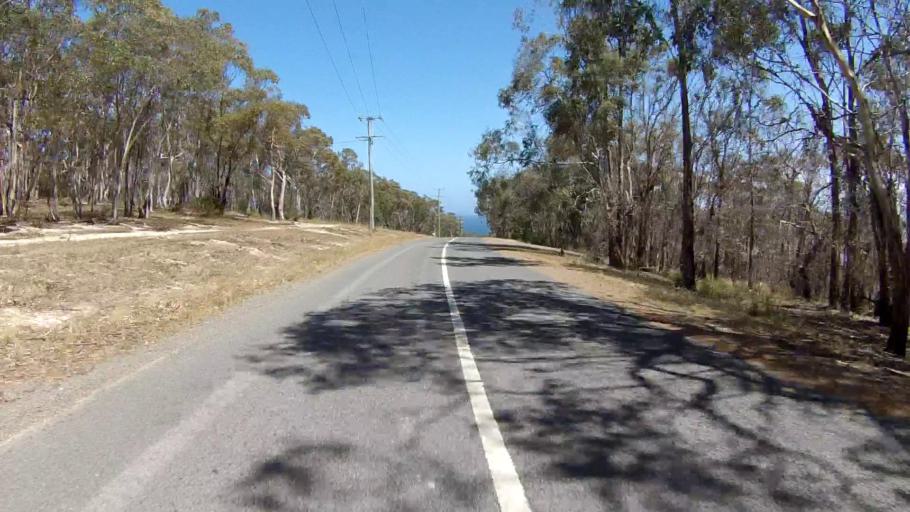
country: AU
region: Tasmania
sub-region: Clarence
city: Sandford
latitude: -43.0192
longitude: 147.4816
